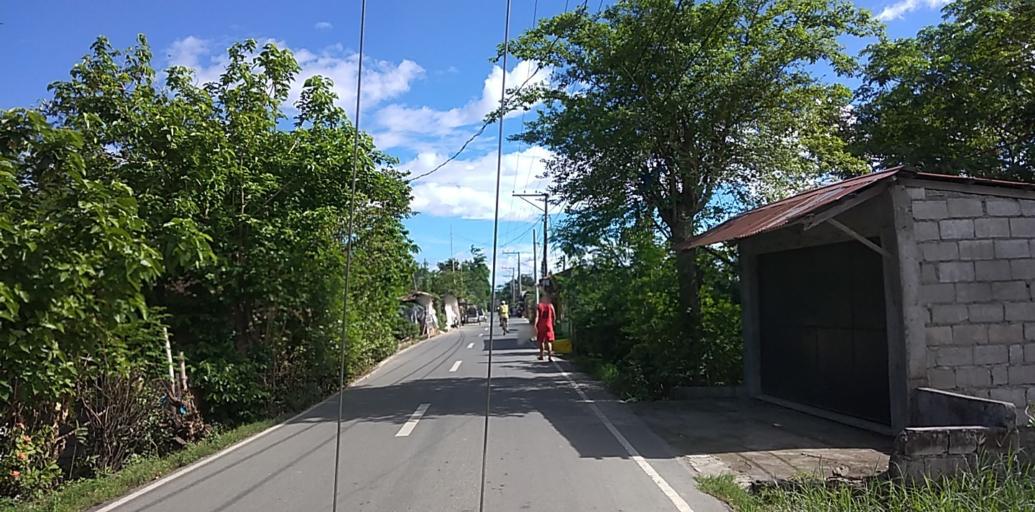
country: PH
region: Central Luzon
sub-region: Province of Pampanga
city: Arayat
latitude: 15.1362
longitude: 120.7856
